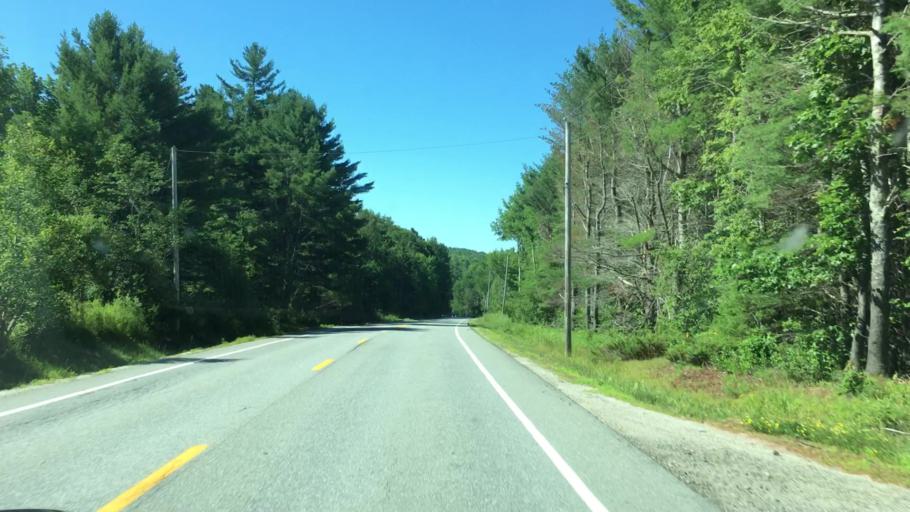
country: US
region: Maine
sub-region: Hancock County
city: Dedham
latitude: 44.6685
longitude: -68.6736
